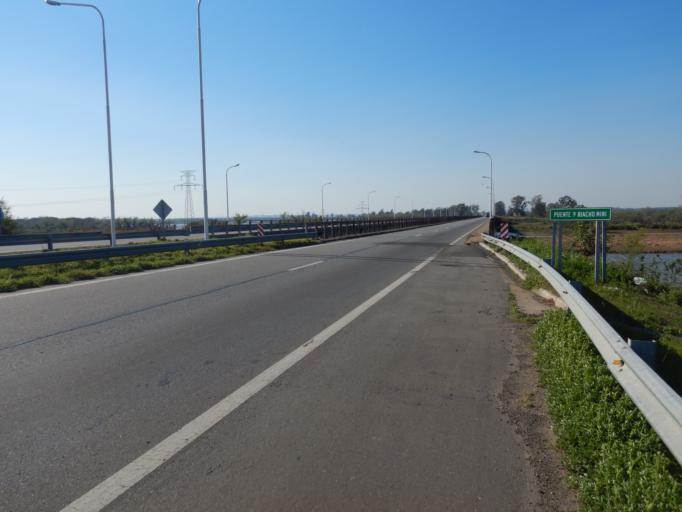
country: AR
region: Entre Rios
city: Parana
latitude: -31.6710
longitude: -60.5800
